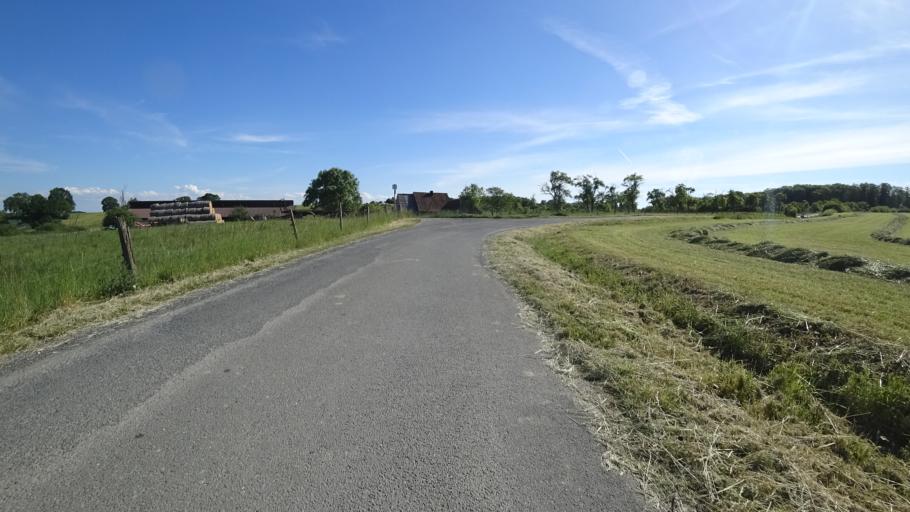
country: DE
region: North Rhine-Westphalia
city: Oelde
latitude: 51.7845
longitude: 8.1962
